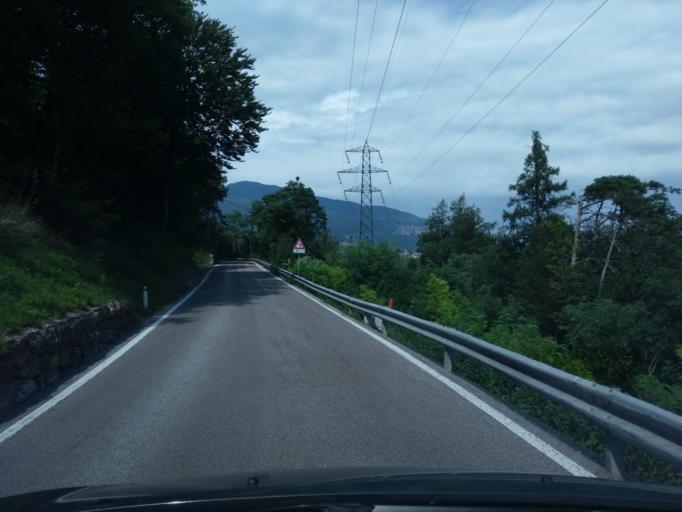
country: IT
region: Trentino-Alto Adige
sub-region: Provincia di Trento
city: Spormaggiore
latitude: 46.2359
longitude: 11.0589
